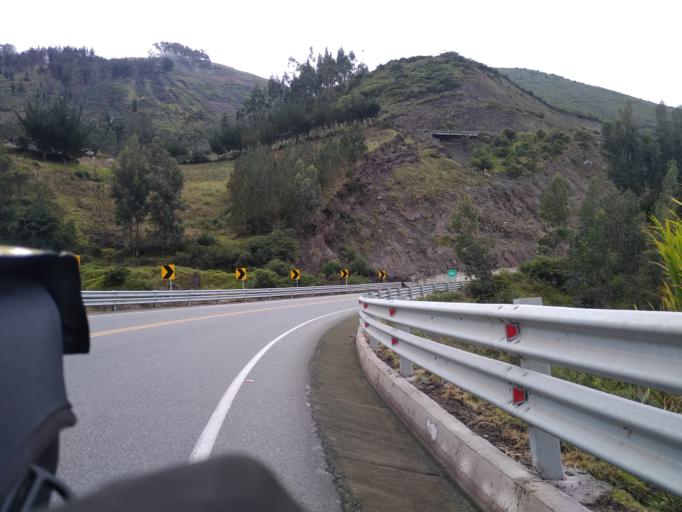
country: EC
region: Chimborazo
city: Guano
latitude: -1.5059
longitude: -78.5243
